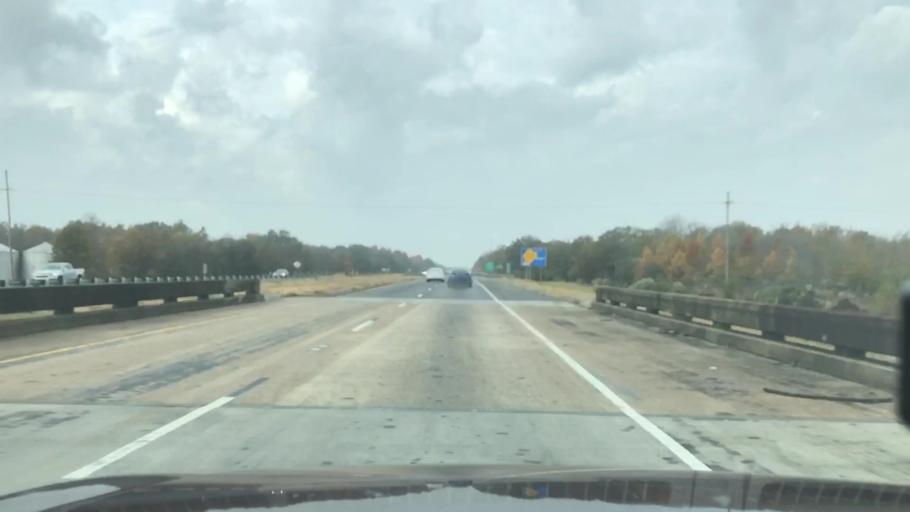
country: US
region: Louisiana
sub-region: Richland Parish
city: Delhi
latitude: 32.4389
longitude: -91.4680
